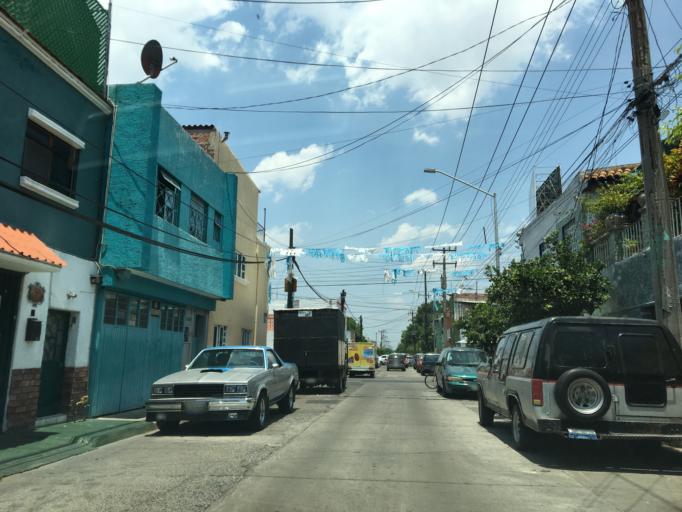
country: MX
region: Jalisco
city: Guadalajara
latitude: 20.6518
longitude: -103.3669
